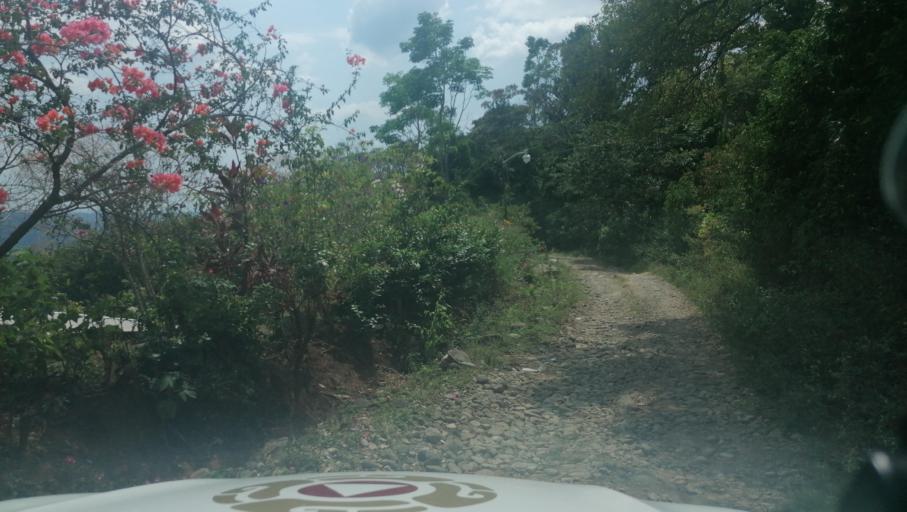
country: MX
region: Chiapas
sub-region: Cacahoatan
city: Benito Juarez
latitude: 15.0585
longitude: -92.2267
